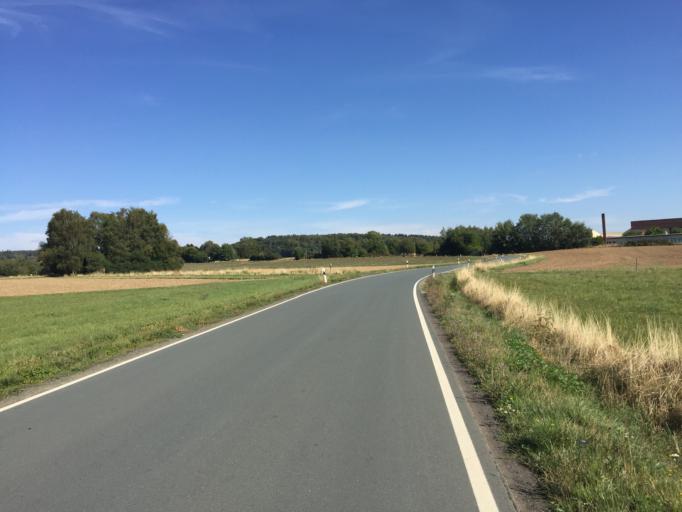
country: DE
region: Hesse
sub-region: Regierungsbezirk Giessen
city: Reiskirchen
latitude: 50.5999
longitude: 8.8397
